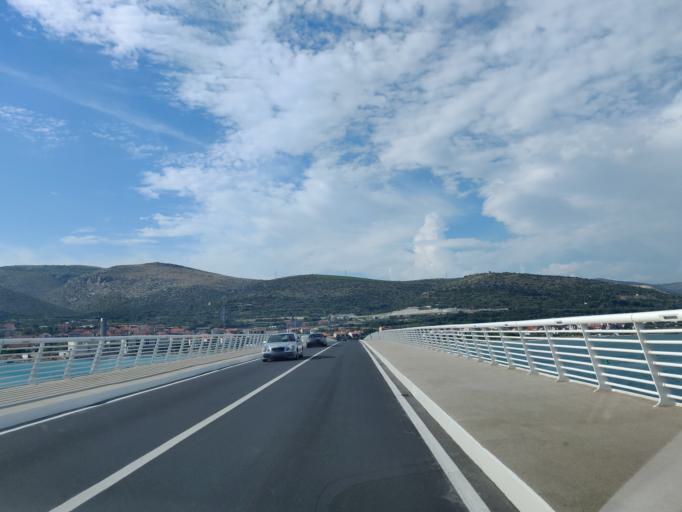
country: HR
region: Splitsko-Dalmatinska
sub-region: Grad Trogir
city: Trogir
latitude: 43.5171
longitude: 16.2651
